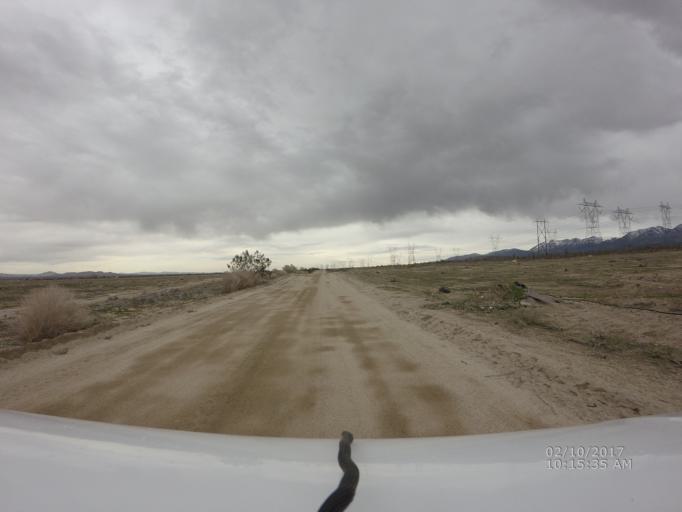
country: US
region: California
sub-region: Los Angeles County
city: Littlerock
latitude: 34.5141
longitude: -117.9649
